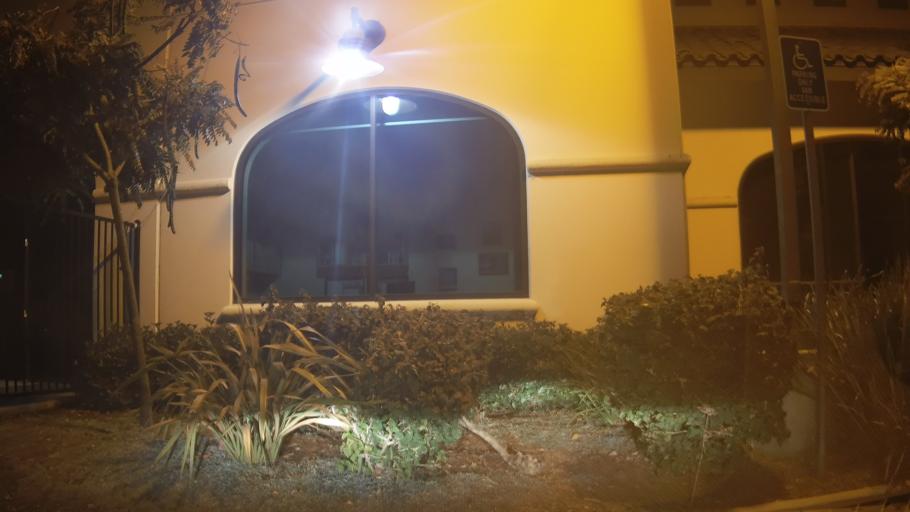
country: US
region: California
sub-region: San Diego County
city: Rancho San Diego
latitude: 32.7359
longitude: -116.9401
